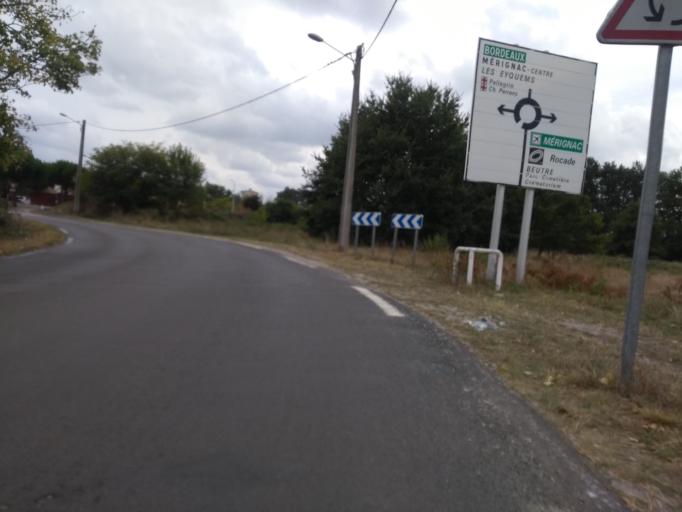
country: FR
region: Aquitaine
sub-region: Departement de la Gironde
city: Pessac
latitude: 44.8201
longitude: -0.6589
